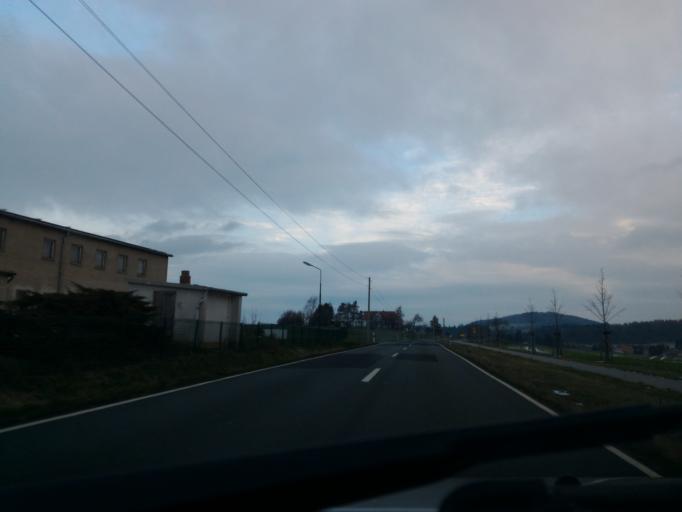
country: DE
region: Saxony
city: Leutersdorf
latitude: 50.9427
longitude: 14.6714
